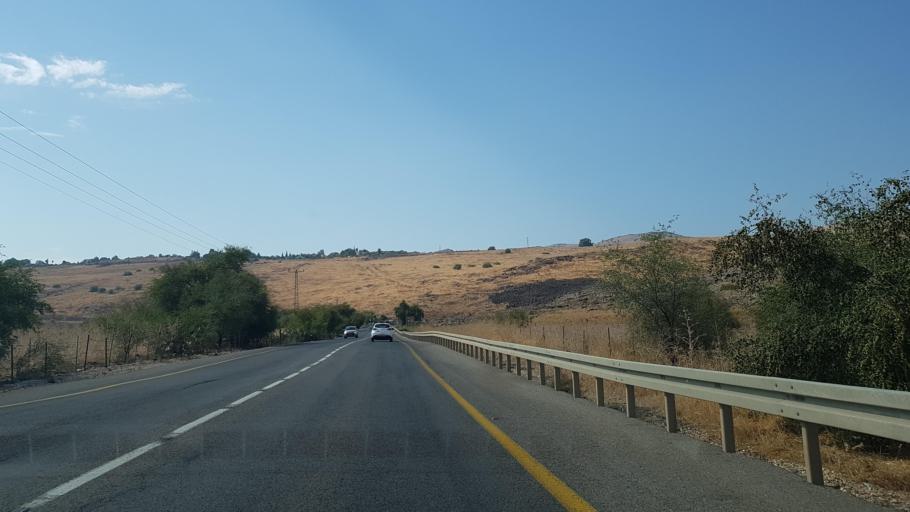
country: IL
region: Northern District
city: Rosh Pinna
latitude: 32.9121
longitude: 35.5690
